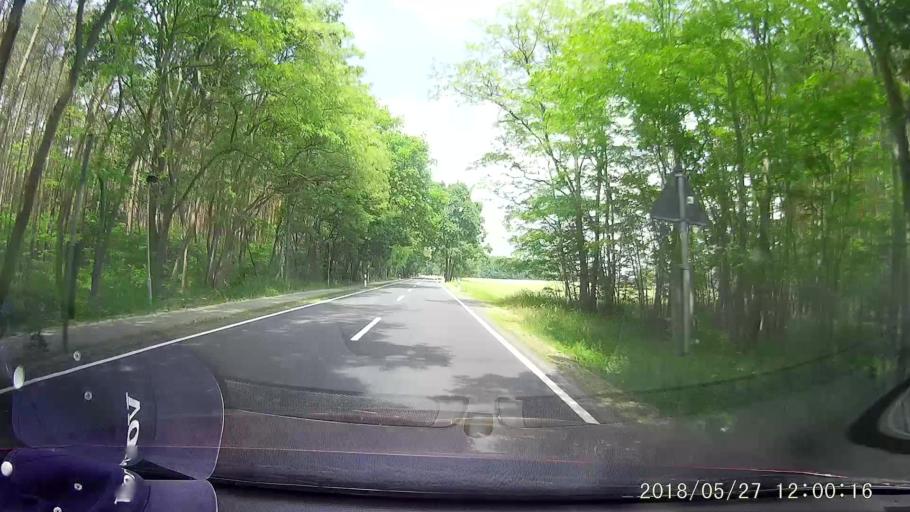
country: DE
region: Saxony
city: Mucka
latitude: 51.3220
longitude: 14.7028
